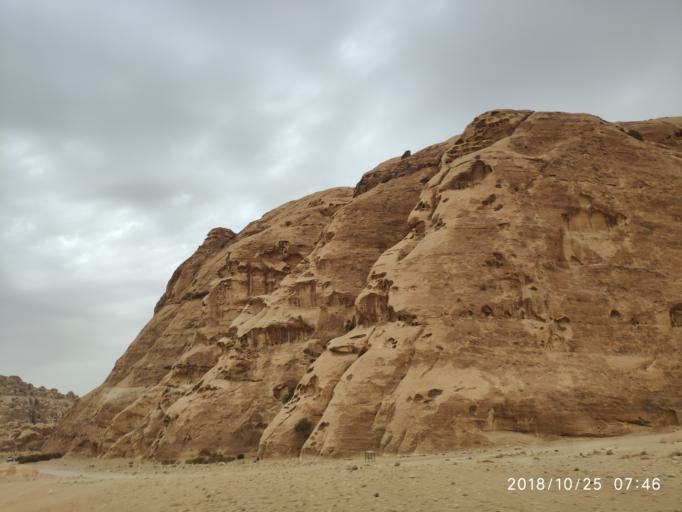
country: JO
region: Ma'an
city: Petra
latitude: 30.3767
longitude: 35.4551
